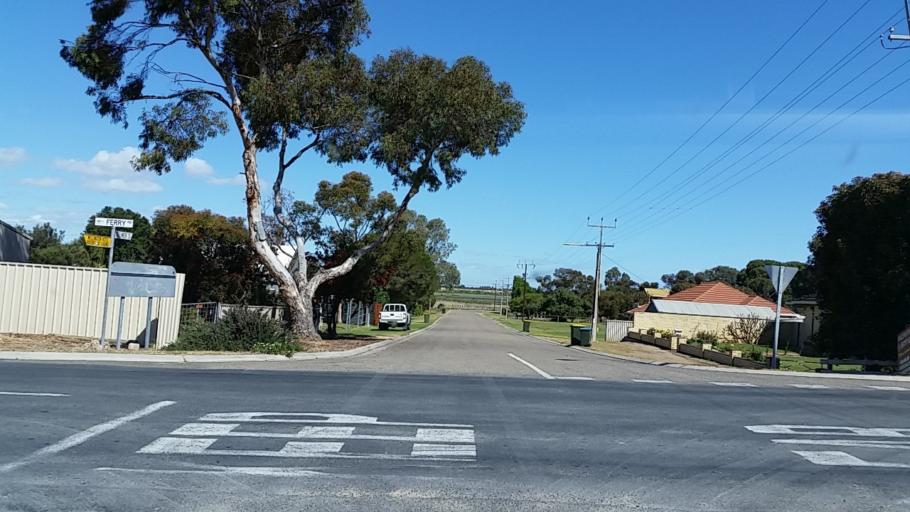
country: AU
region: South Australia
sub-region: Murray Bridge
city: Tailem Bend
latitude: -35.3318
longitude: 139.3839
